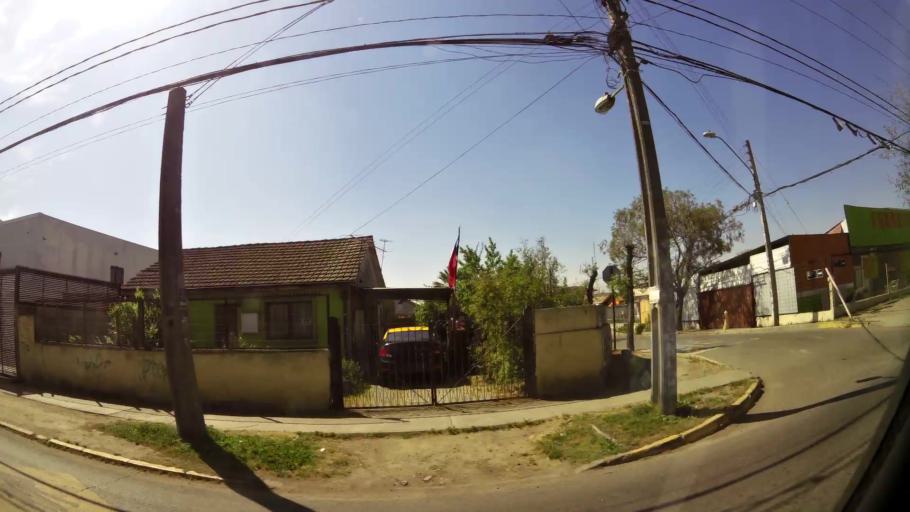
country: CL
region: Santiago Metropolitan
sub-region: Provincia de Santiago
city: Lo Prado
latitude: -33.5026
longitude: -70.7277
